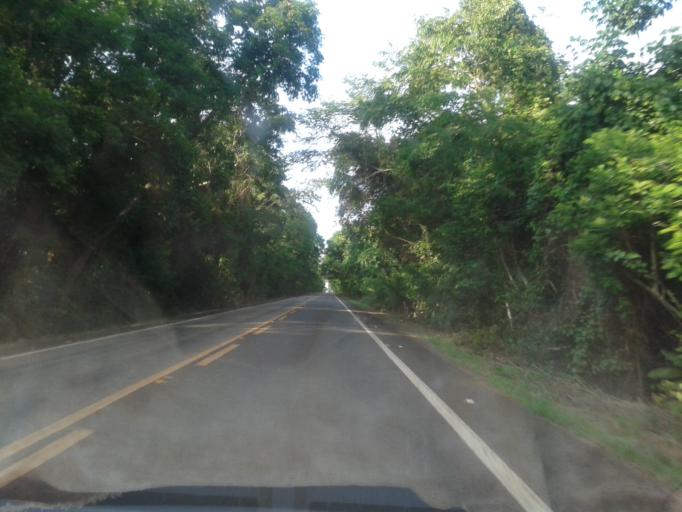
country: BR
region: Goias
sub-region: Crixas
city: Crixas
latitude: -13.9750
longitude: -50.3219
